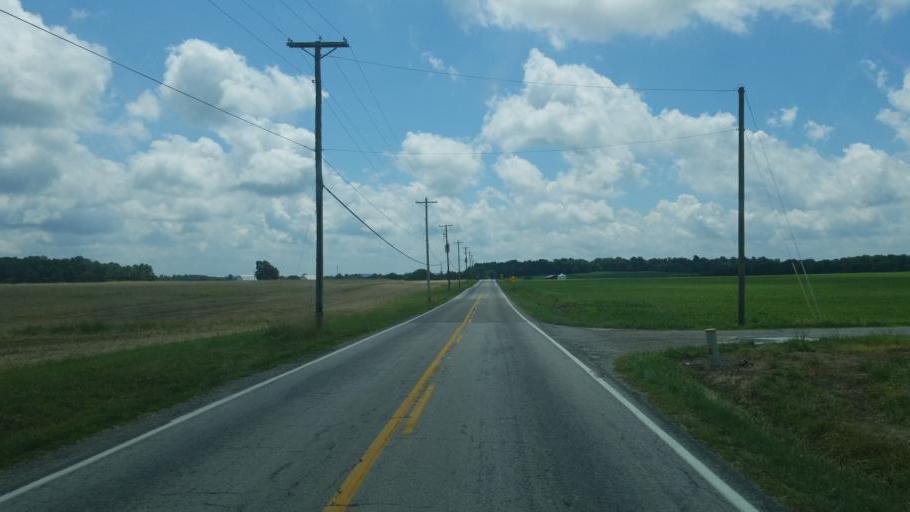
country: US
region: Ohio
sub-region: Highland County
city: Greenfield
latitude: 39.2487
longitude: -83.4399
